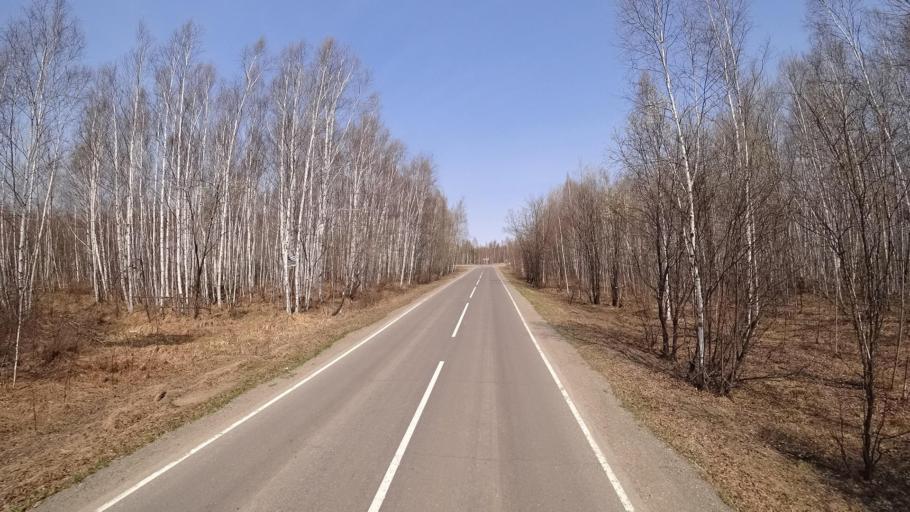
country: RU
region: Khabarovsk Krai
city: Selikhino
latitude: 50.3946
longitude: 137.3738
